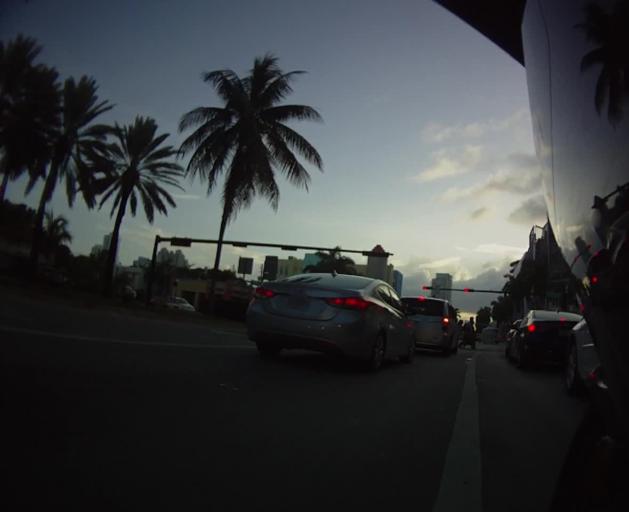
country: US
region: Florida
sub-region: Miami-Dade County
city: Miami Beach
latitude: 25.7747
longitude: -80.1325
